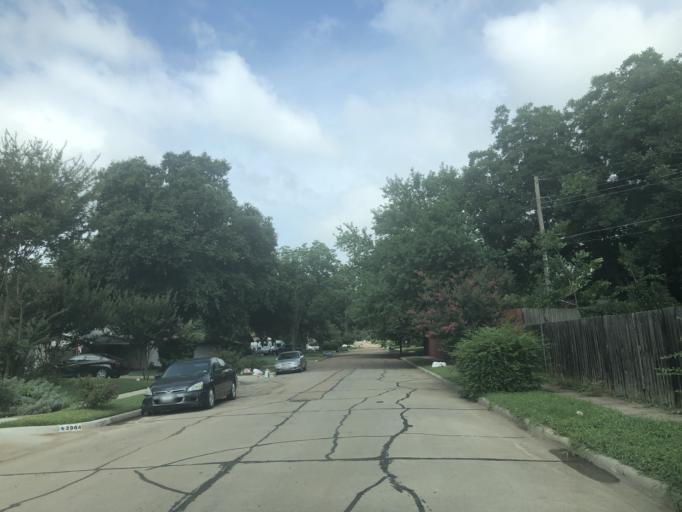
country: US
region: Texas
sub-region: Dallas County
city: Irving
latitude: 32.7966
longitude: -96.9712
